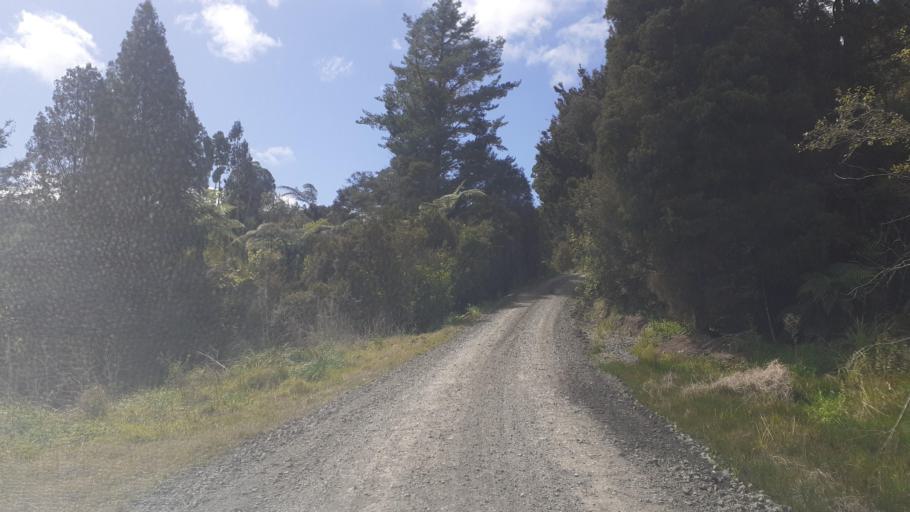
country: NZ
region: Northland
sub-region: Far North District
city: Moerewa
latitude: -35.5838
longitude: 173.9378
